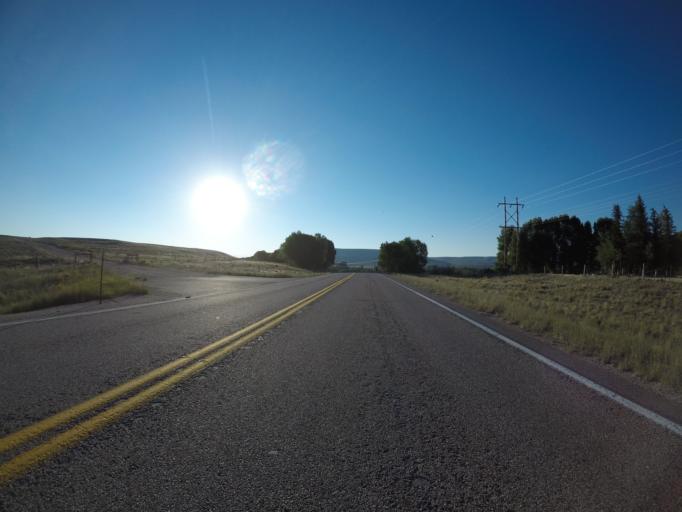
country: US
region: Wyoming
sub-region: Sublette County
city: Marbleton
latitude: 42.5699
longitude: -109.9580
